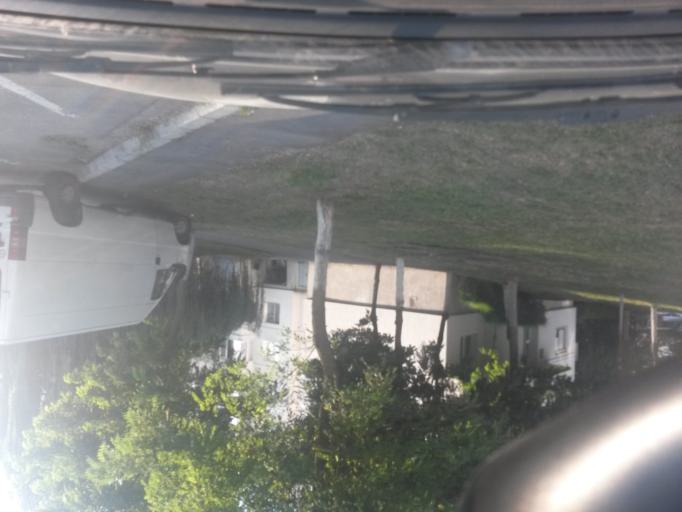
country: RO
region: Mures
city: Targu-Mures
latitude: 46.5320
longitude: 24.5781
